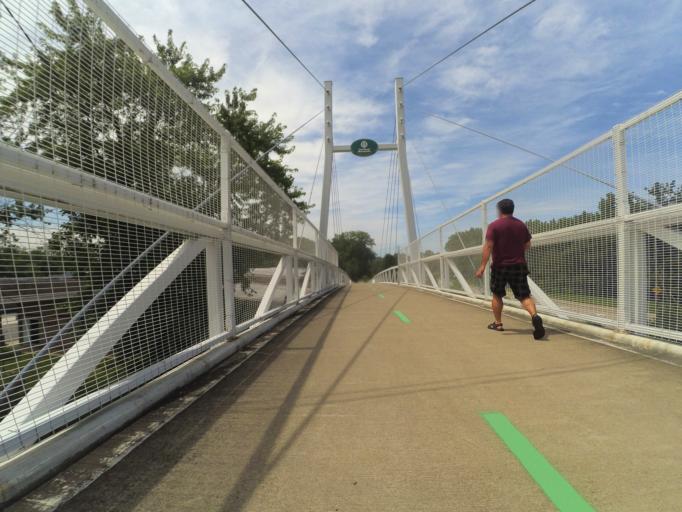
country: US
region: Ohio
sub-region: Cuyahoga County
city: Garfield Heights
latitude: 41.4168
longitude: -81.6365
